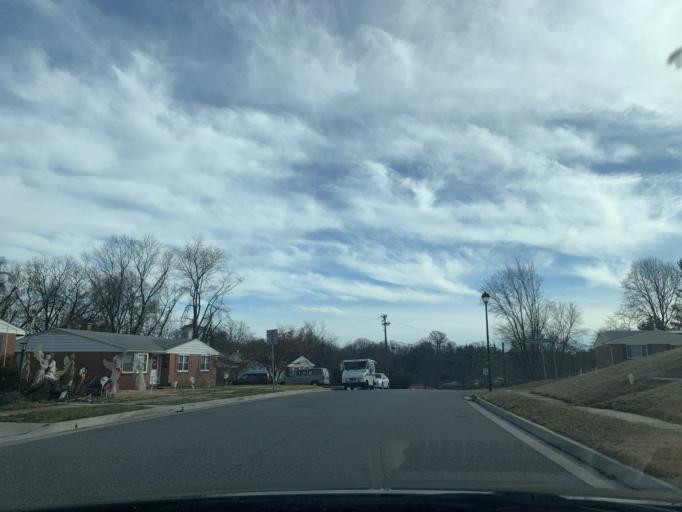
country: US
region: Maryland
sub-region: Baltimore County
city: Pikesville
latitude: 39.3738
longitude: -76.7514
